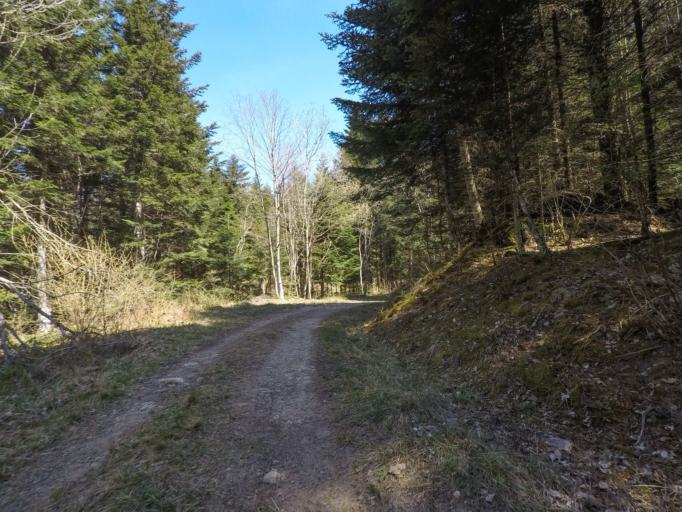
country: FR
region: Rhone-Alpes
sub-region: Departement de la Haute-Savoie
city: Beaumont
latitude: 46.1102
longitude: 6.1446
